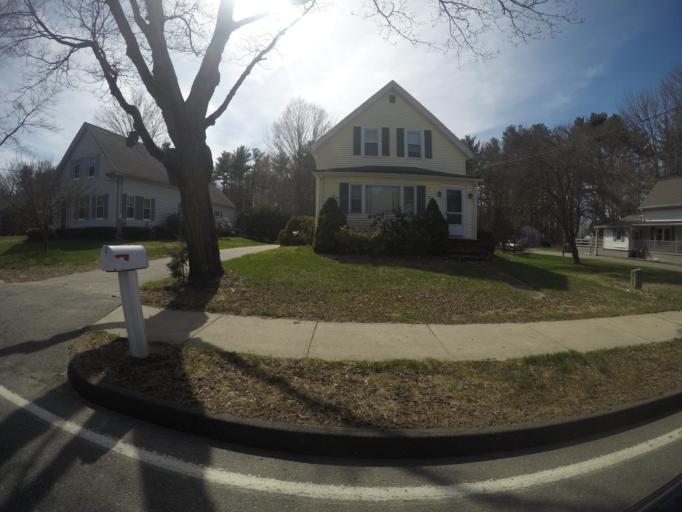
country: US
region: Massachusetts
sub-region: Bristol County
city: Easton
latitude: 42.0389
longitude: -71.0679
